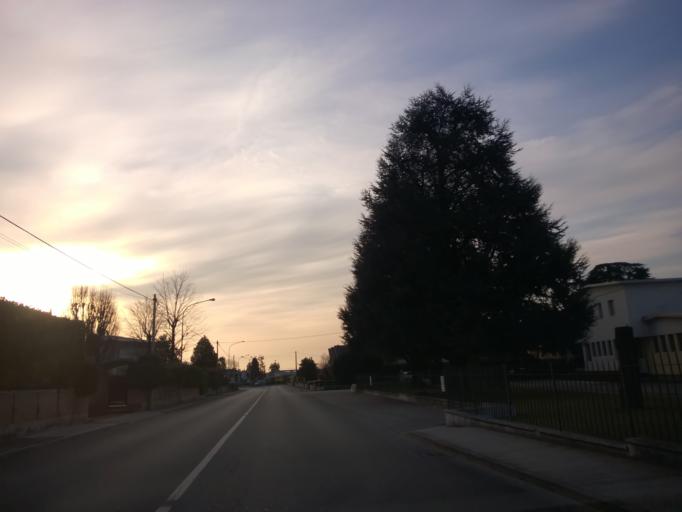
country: IT
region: Veneto
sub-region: Provincia di Vicenza
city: Thiene
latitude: 45.7174
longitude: 11.4690
